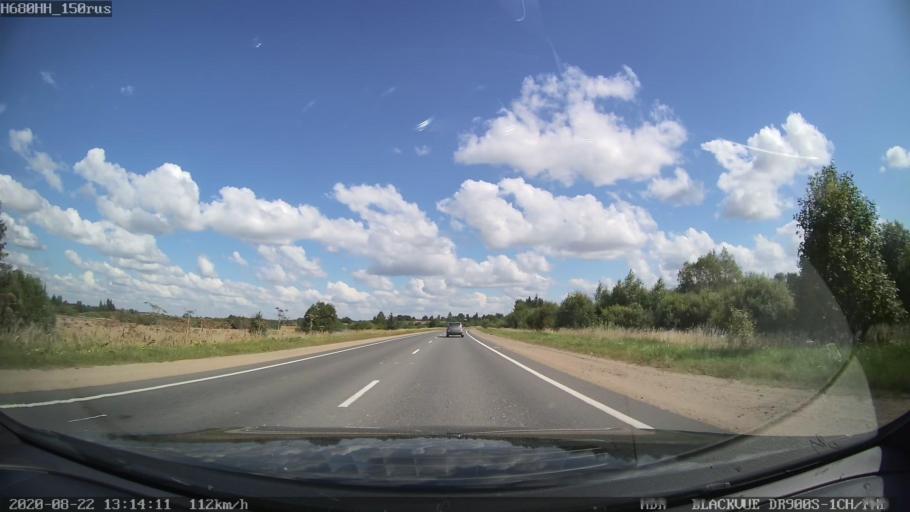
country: RU
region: Tverskaya
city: Bezhetsk
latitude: 57.7547
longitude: 36.5946
